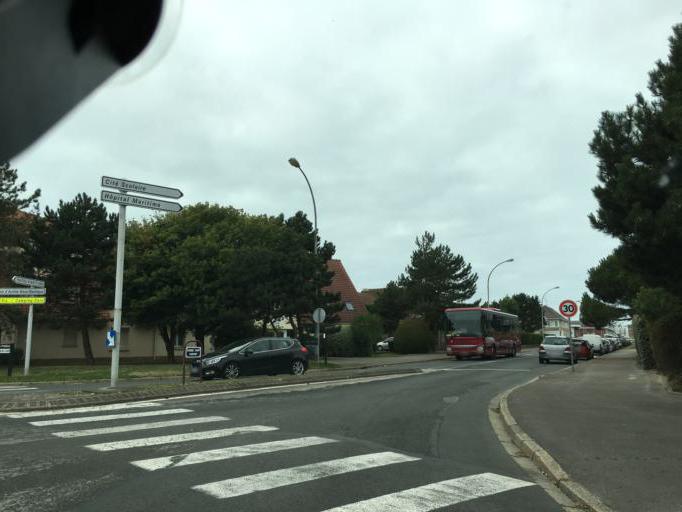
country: FR
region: Nord-Pas-de-Calais
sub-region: Departement du Pas-de-Calais
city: Berck-Plage
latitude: 50.3988
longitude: 1.5684
